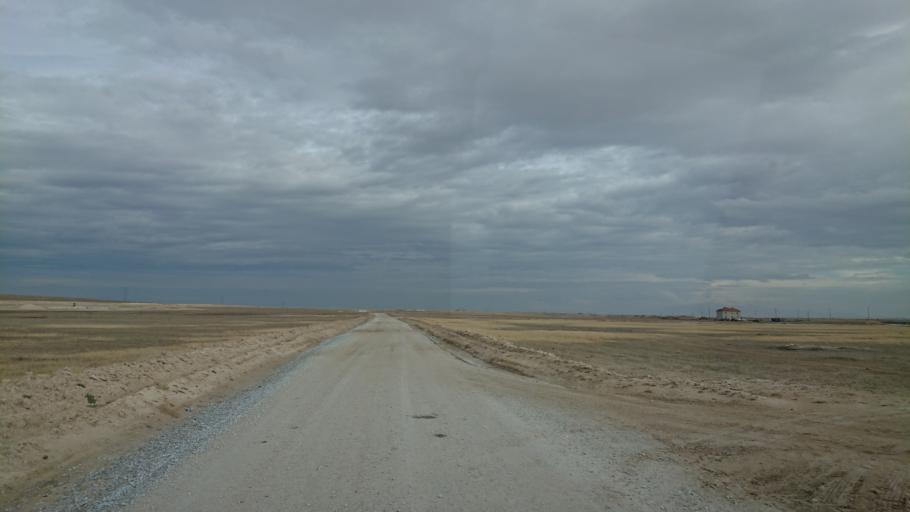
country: TR
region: Aksaray
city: Sultanhani
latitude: 38.1333
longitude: 33.5494
